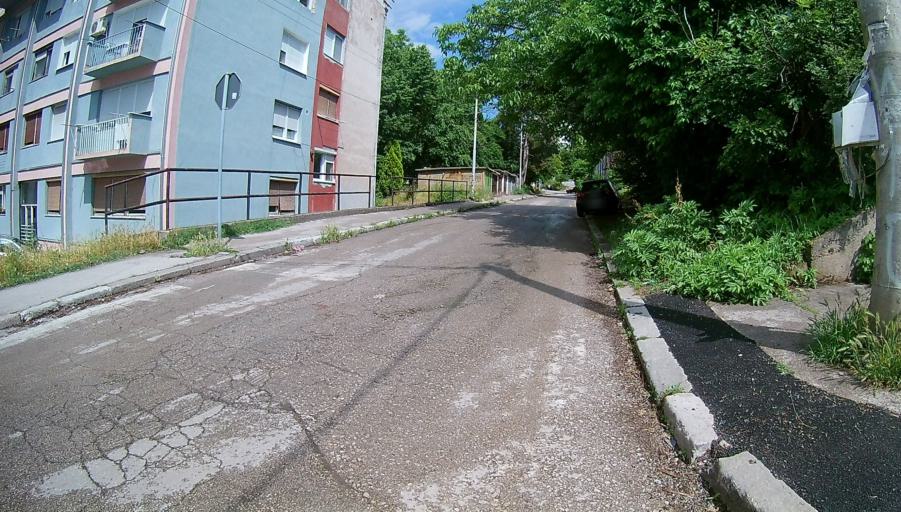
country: RS
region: Central Serbia
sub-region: Nisavski Okrug
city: Nis
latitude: 43.3089
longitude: 21.8973
